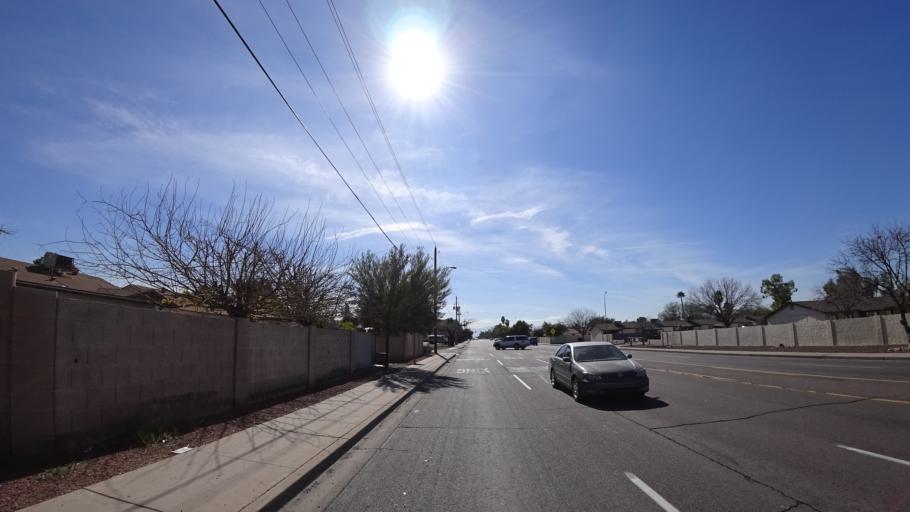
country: US
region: Arizona
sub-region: Maricopa County
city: Glendale
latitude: 33.4901
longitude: -112.2032
